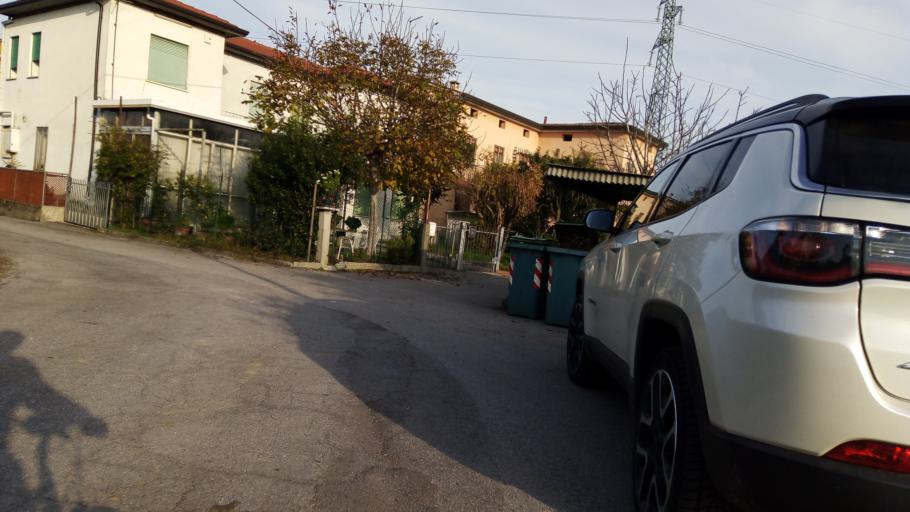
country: IT
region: Veneto
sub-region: Provincia di Padova
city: Abano Terme
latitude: 45.3667
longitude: 11.7994
